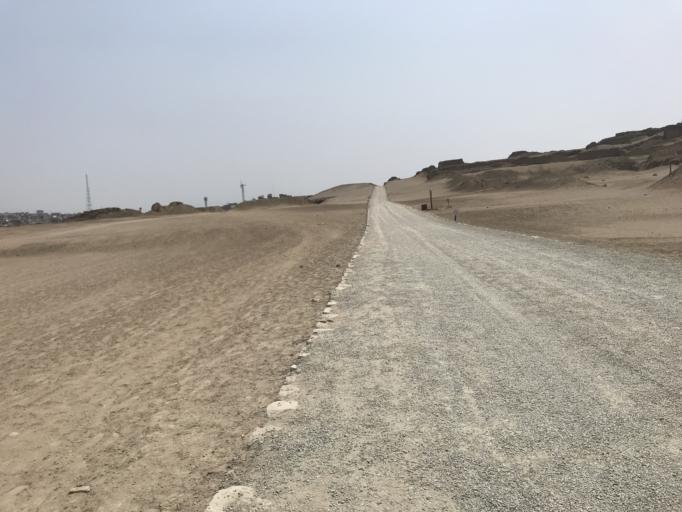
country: PE
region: Lima
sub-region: Lima
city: Punta Hermosa
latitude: -12.2557
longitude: -76.9010
